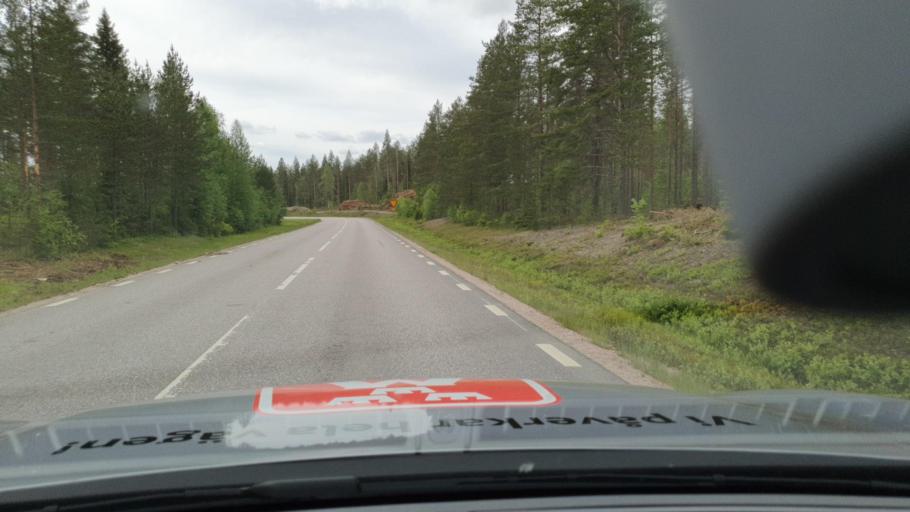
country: SE
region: Norrbotten
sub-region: Kalix Kommun
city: Kalix
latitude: 65.8532
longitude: 23.4701
